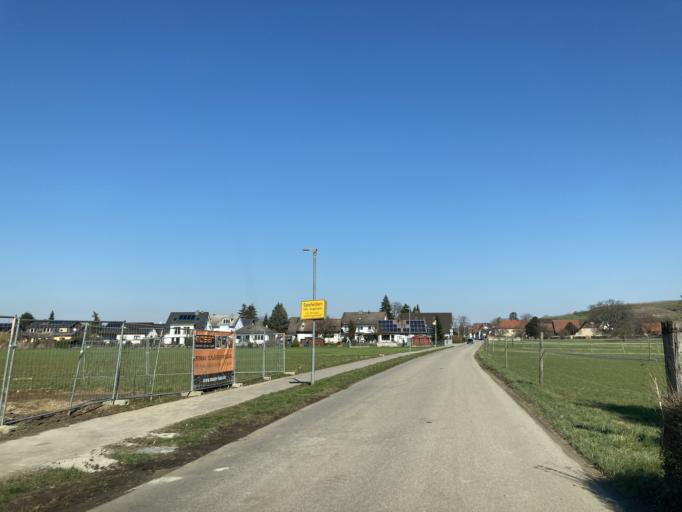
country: DE
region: Baden-Wuerttemberg
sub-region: Freiburg Region
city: Buggingen
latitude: 47.8546
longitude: 7.6403
